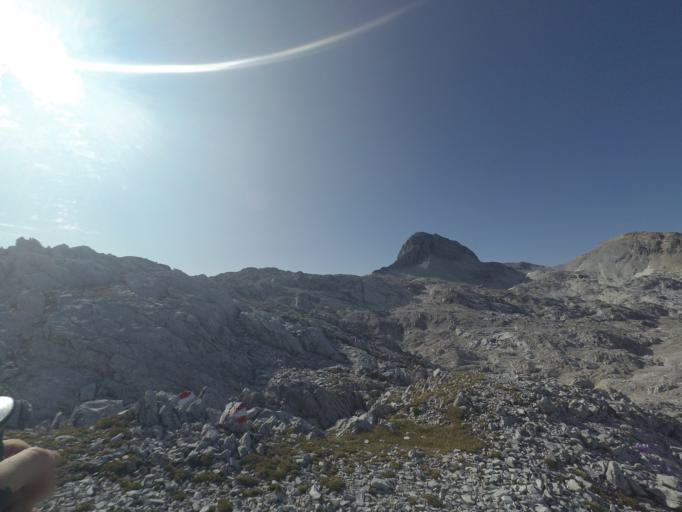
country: AT
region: Salzburg
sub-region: Politischer Bezirk Sankt Johann im Pongau
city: Kleinarl
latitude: 47.2137
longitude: 13.4009
